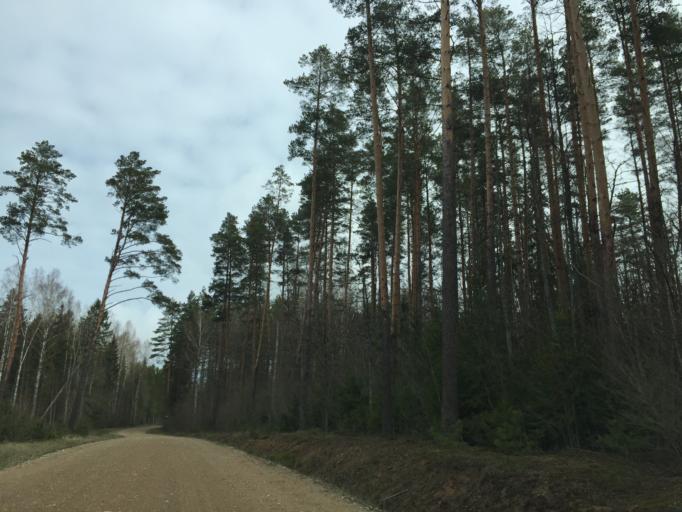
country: LV
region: Salacgrivas
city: Salacgriva
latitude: 57.5134
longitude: 24.4136
